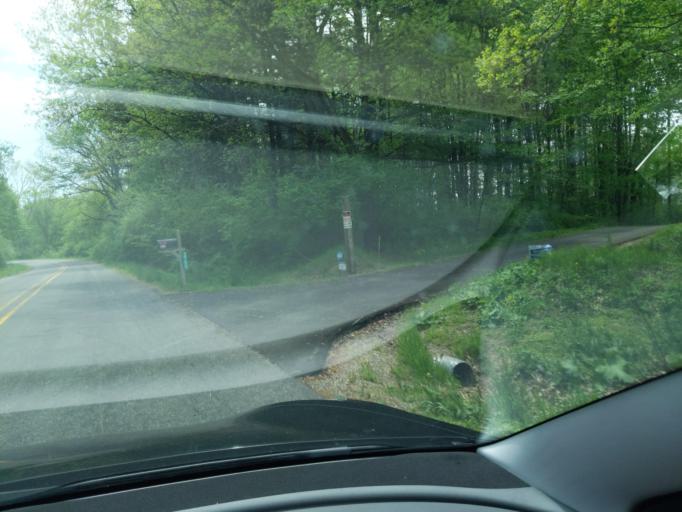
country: US
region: Michigan
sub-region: Ingham County
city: Stockbridge
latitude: 42.4769
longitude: -84.2321
